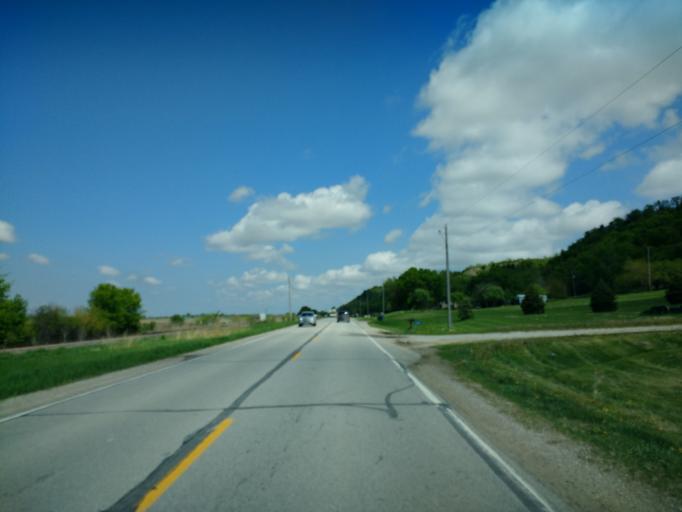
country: US
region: Iowa
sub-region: Harrison County
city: Missouri Valley
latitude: 41.4758
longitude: -95.8821
